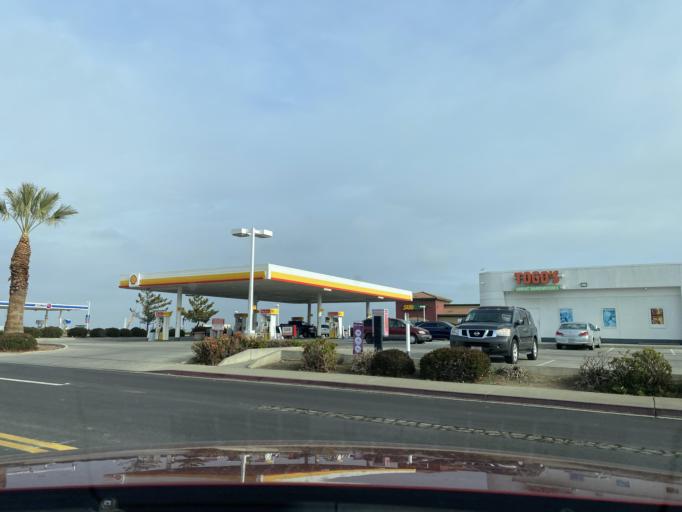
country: US
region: California
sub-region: Colusa County
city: Williams
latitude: 39.1578
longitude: -122.1403
